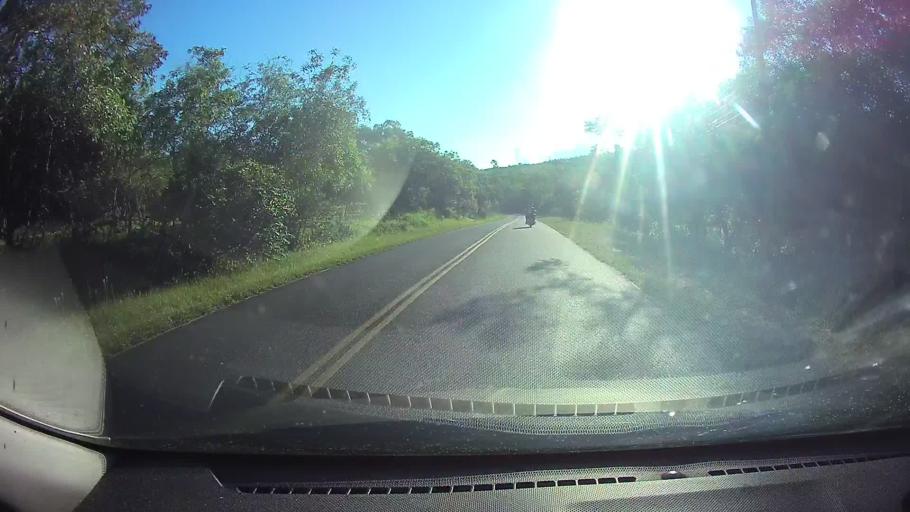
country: PY
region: Cordillera
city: Emboscada
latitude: -25.1742
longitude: -57.2860
